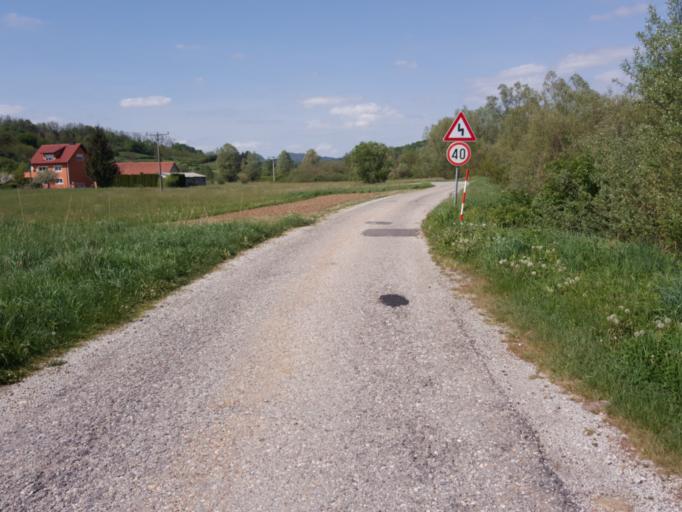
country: HR
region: Varazdinska
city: Lepoglava
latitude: 46.2280
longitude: 15.9654
